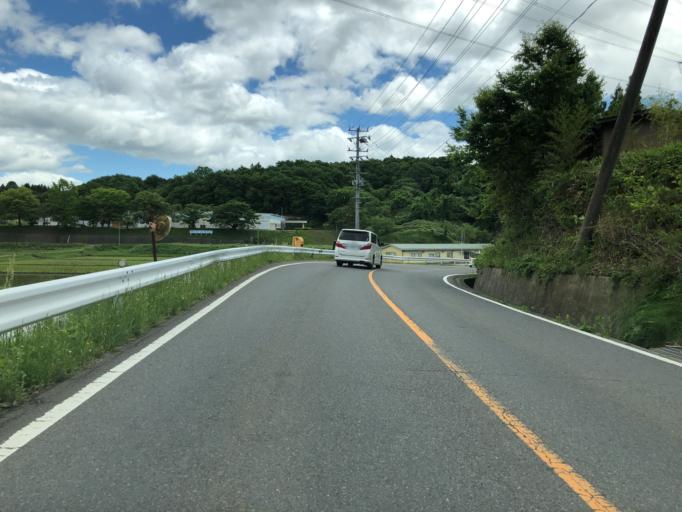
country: JP
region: Fukushima
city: Motomiya
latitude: 37.5105
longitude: 140.4294
